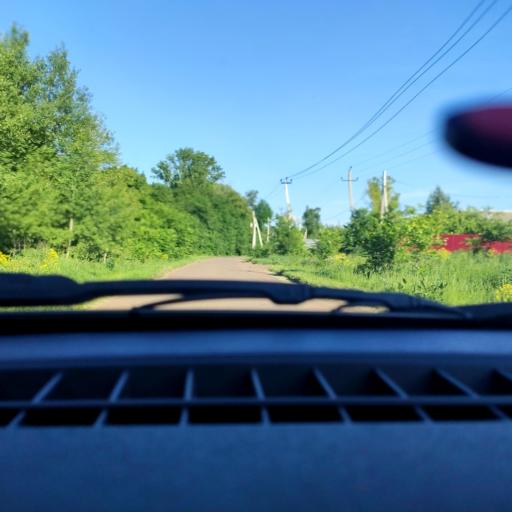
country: RU
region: Bashkortostan
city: Avdon
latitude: 54.4650
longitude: 55.8335
